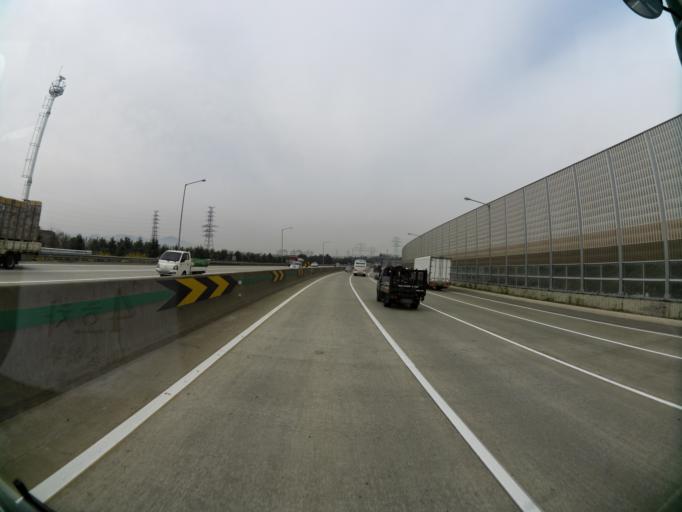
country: KR
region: Gyeongsangbuk-do
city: Gyeongsan-si
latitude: 35.8707
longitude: 128.7495
